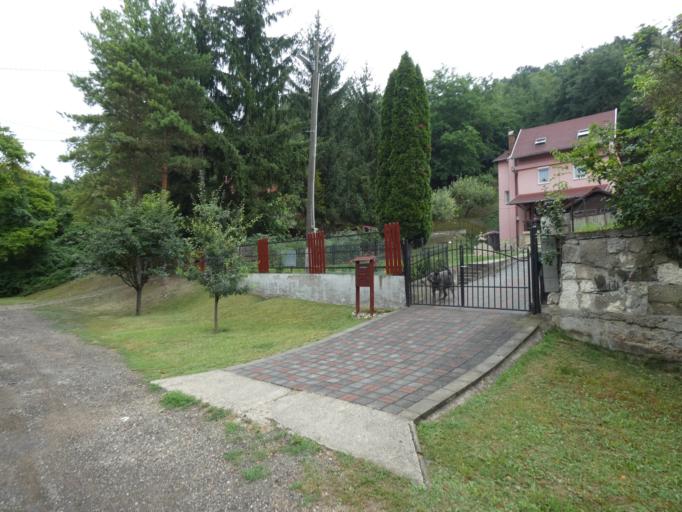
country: HU
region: Pest
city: Szob
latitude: 47.8137
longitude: 18.9010
